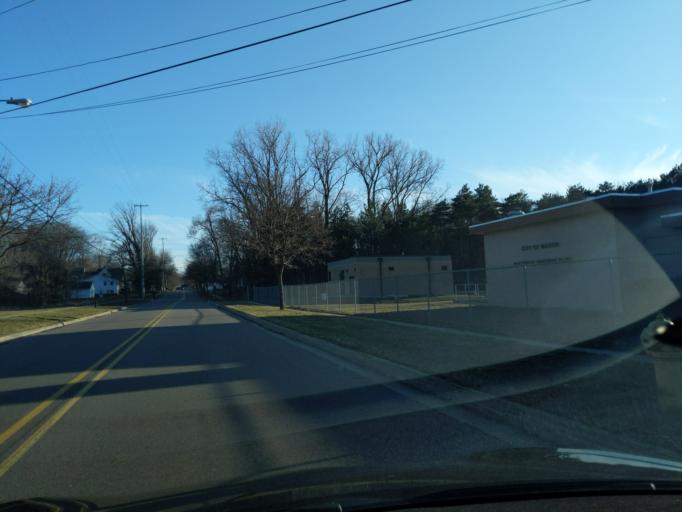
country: US
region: Michigan
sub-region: Ingham County
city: Mason
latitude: 42.5872
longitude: -84.4431
